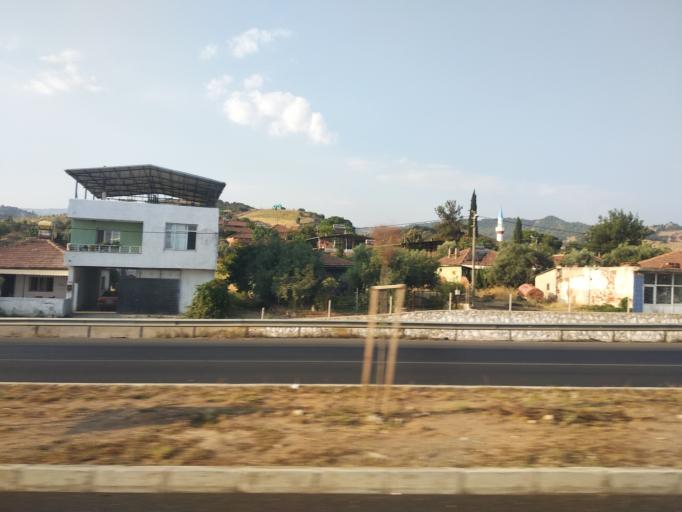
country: TR
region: Manisa
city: Ahmetli
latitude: 38.5093
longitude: 27.9807
